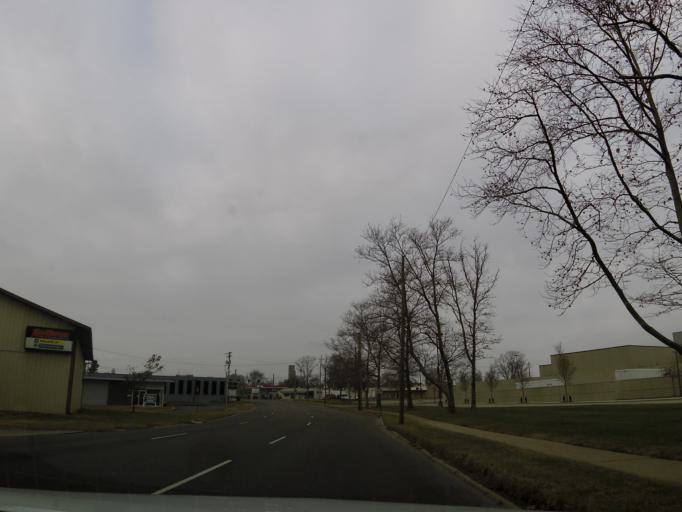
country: US
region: Indiana
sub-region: Bartholomew County
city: Columbus
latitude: 39.2013
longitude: -85.9114
